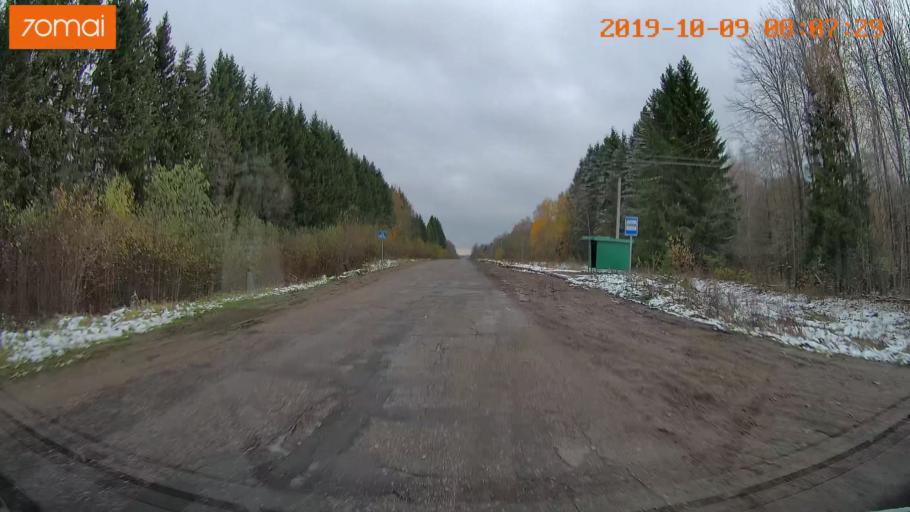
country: RU
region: Jaroslavl
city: Kukoboy
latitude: 58.6981
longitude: 40.0812
